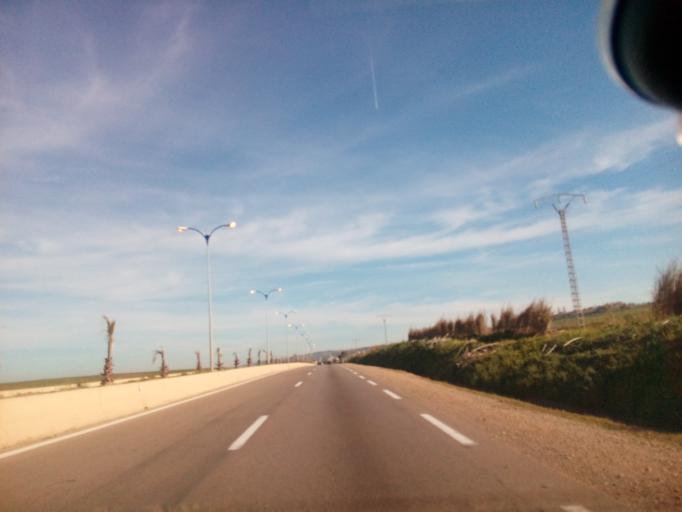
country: DZ
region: Mostaganem
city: Mostaganem
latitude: 35.8203
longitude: -0.0187
